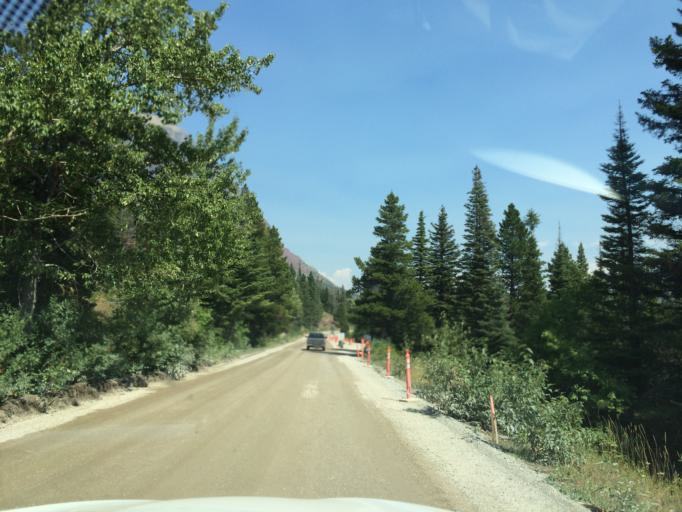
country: US
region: Montana
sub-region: Glacier County
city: Browning
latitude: 48.6740
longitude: -113.6099
